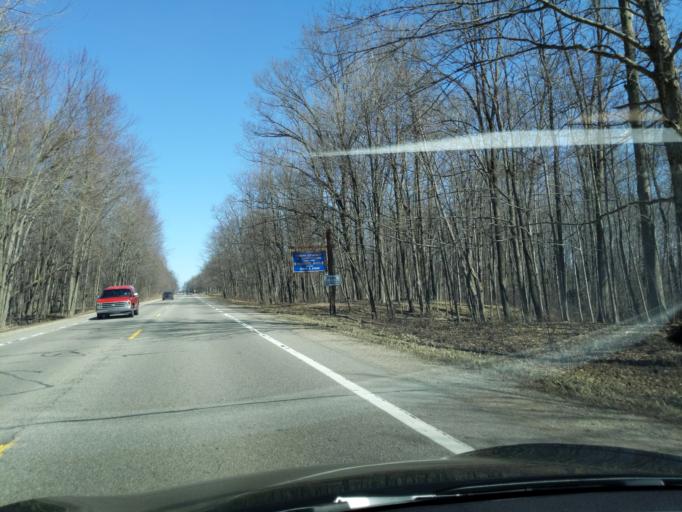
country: US
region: Michigan
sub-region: Ionia County
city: Lake Odessa
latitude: 42.7328
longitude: -85.0860
